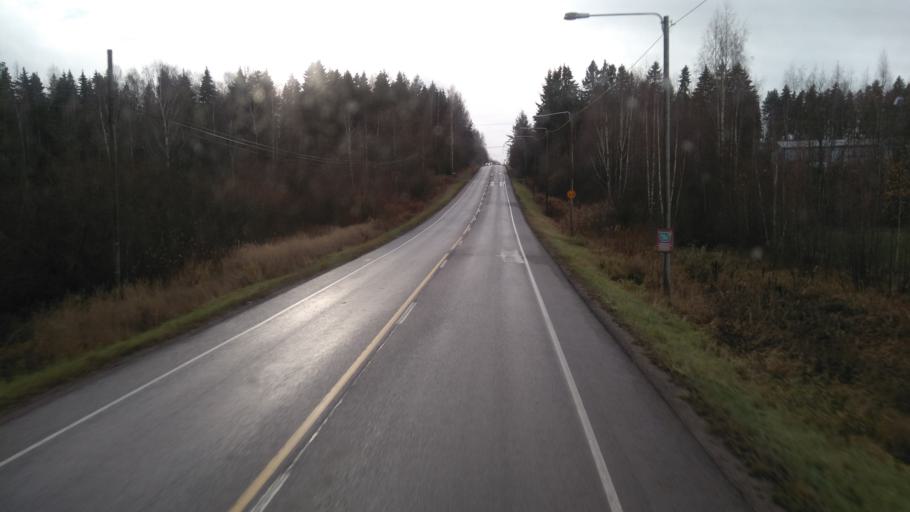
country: FI
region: Uusimaa
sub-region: Porvoo
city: Porvoo
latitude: 60.4072
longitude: 25.6933
